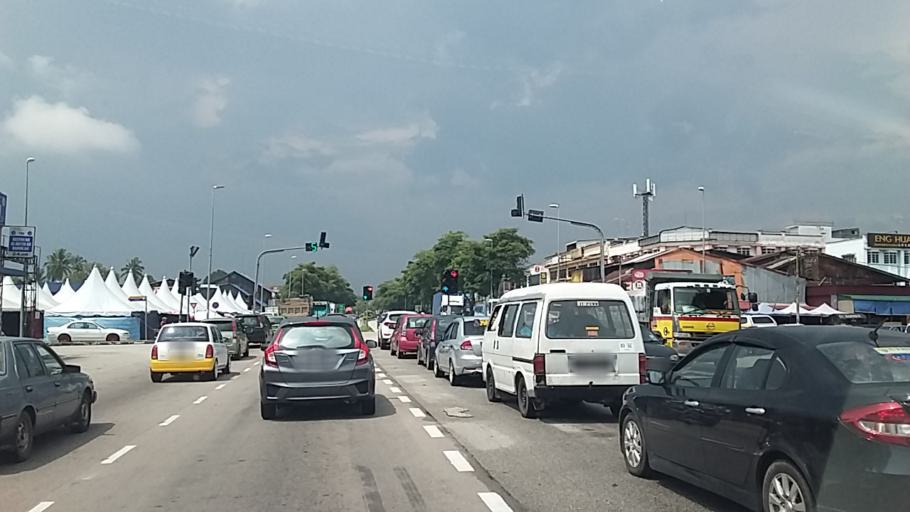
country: MY
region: Johor
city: Parit Raja
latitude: 1.8653
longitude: 103.1116
